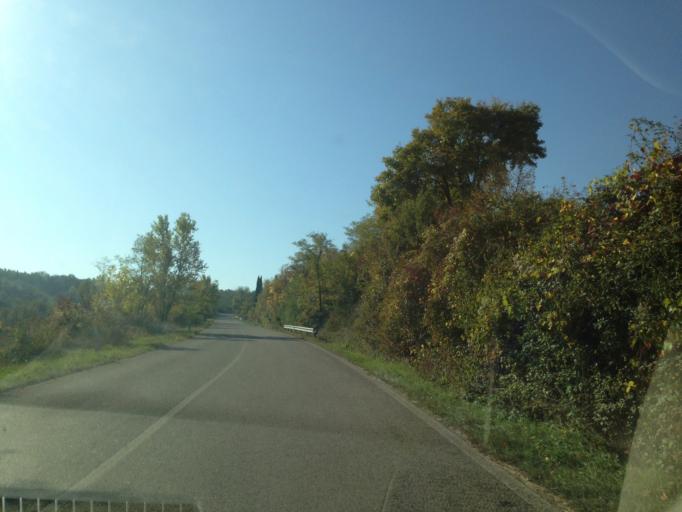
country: IT
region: Tuscany
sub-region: Provincia di Siena
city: Castellina in Chianti
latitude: 43.4826
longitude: 11.2979
